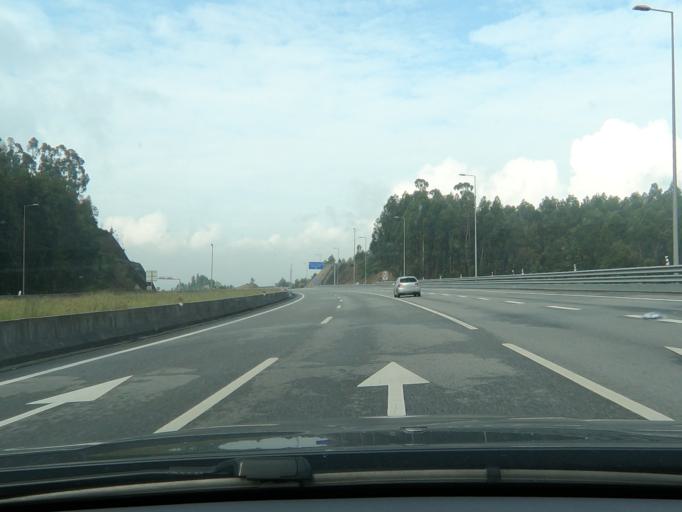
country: PT
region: Porto
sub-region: Gondomar
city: Foz do Sousa
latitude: 41.1019
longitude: -8.4542
